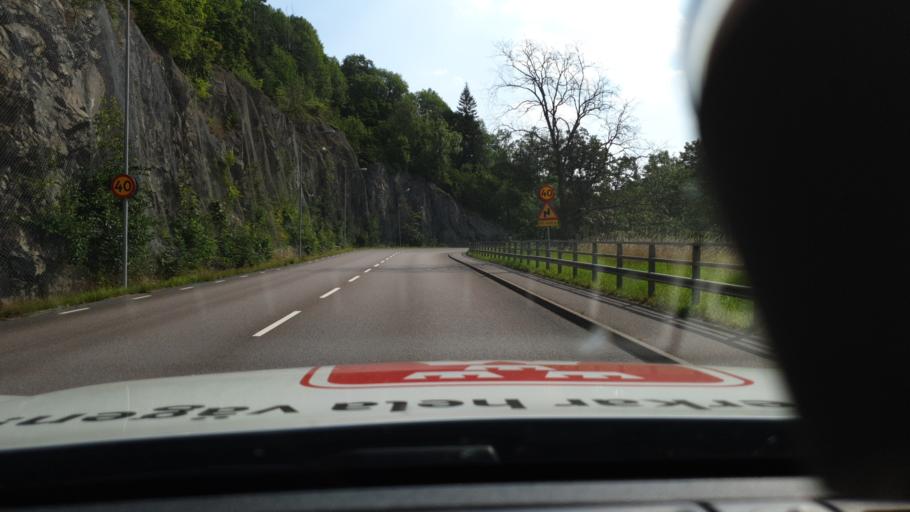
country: SE
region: Joenkoeping
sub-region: Jonkopings Kommun
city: Huskvarna
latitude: 57.7859
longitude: 14.2946
